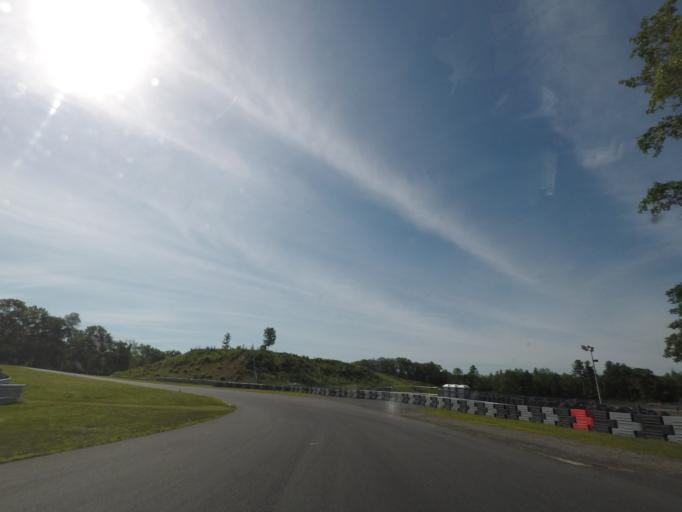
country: US
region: Connecticut
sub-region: Windham County
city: Thompson
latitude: 41.9806
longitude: -71.8238
